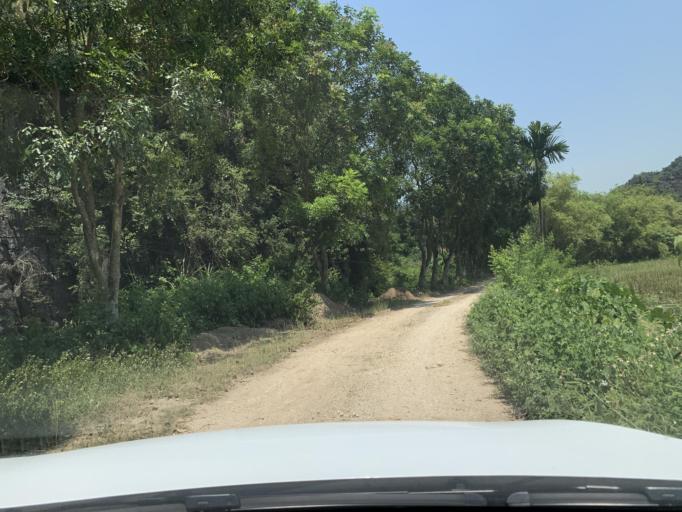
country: VN
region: Ninh Binh
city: Thanh Pho Ninh Binh
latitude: 20.2224
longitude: 105.9287
